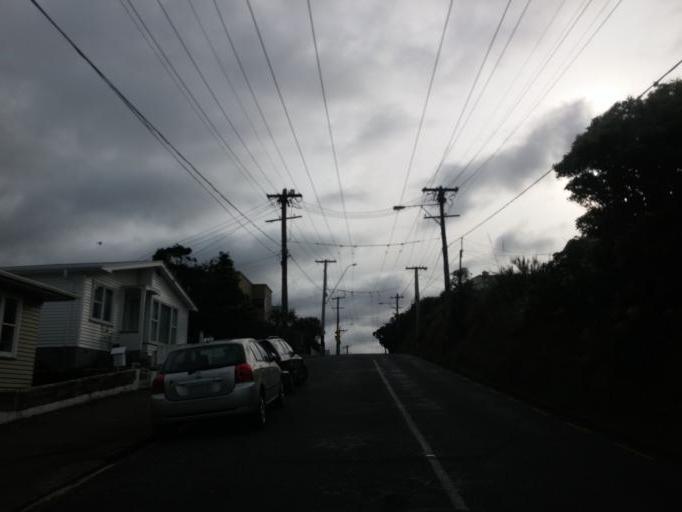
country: NZ
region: Wellington
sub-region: Wellington City
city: Brooklyn
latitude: -41.3115
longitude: 174.7660
